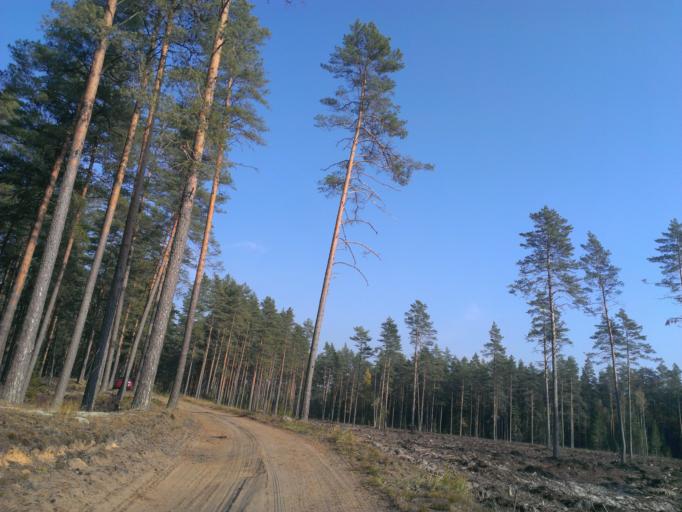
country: LV
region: Garkalne
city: Garkalne
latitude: 57.0169
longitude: 24.4722
